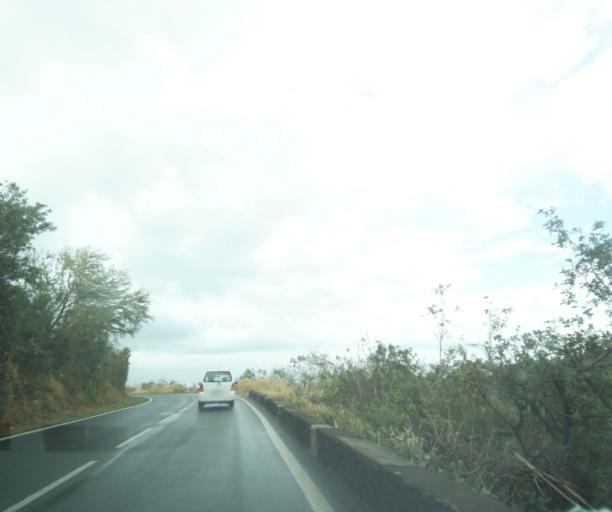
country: RE
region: Reunion
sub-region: Reunion
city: Saint-Paul
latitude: -21.0344
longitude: 55.2798
